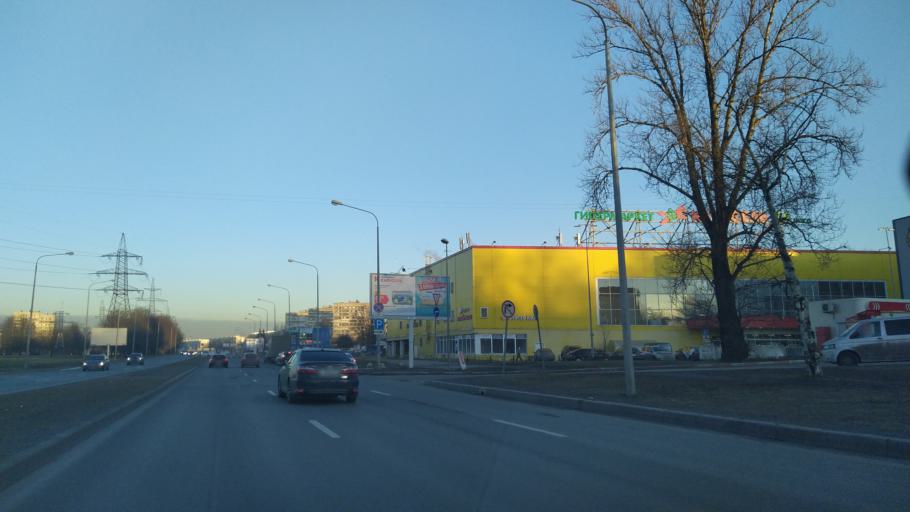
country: RU
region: Leningrad
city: Kalininskiy
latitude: 59.9760
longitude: 30.4061
